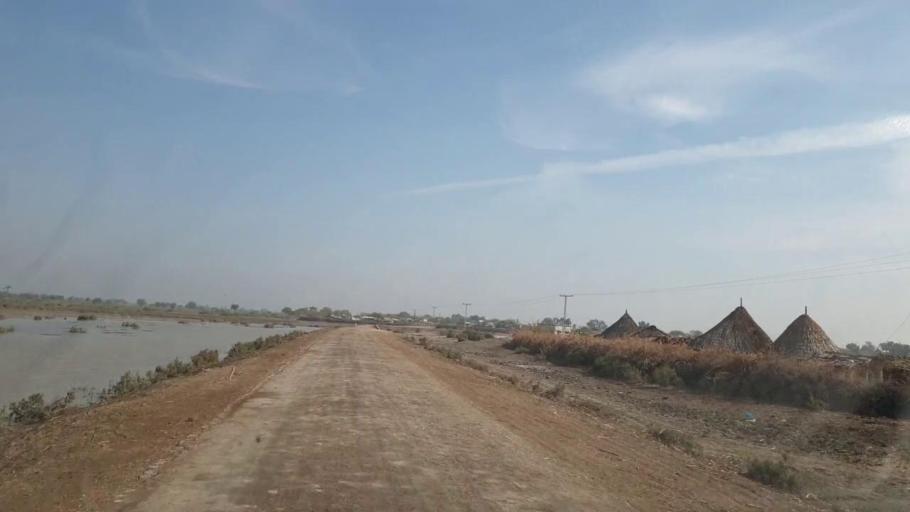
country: PK
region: Sindh
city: Mirpur Khas
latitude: 25.5150
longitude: 69.0968
